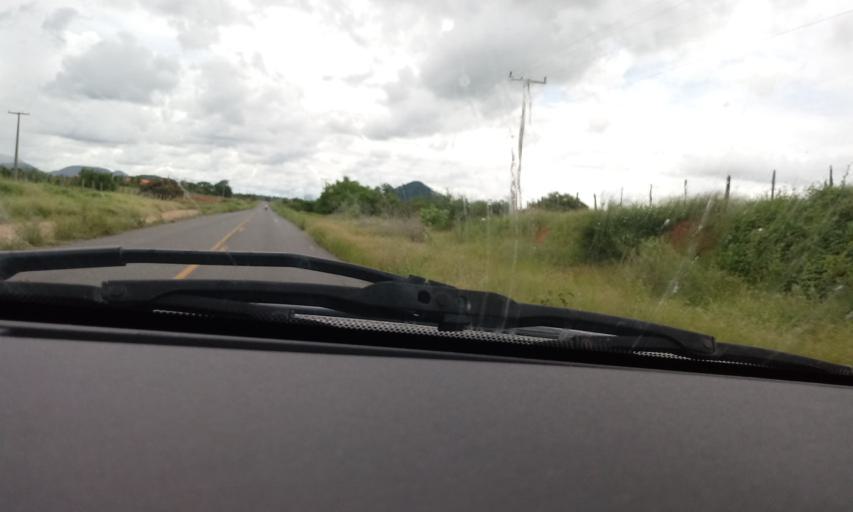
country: BR
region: Bahia
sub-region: Guanambi
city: Guanambi
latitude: -14.0914
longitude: -42.8732
